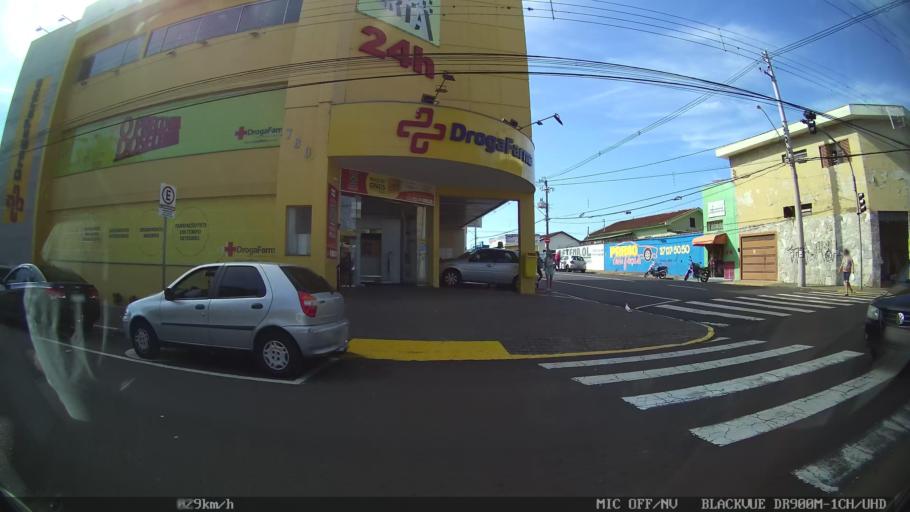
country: BR
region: Sao Paulo
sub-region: Franca
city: Franca
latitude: -20.5321
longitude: -47.4186
